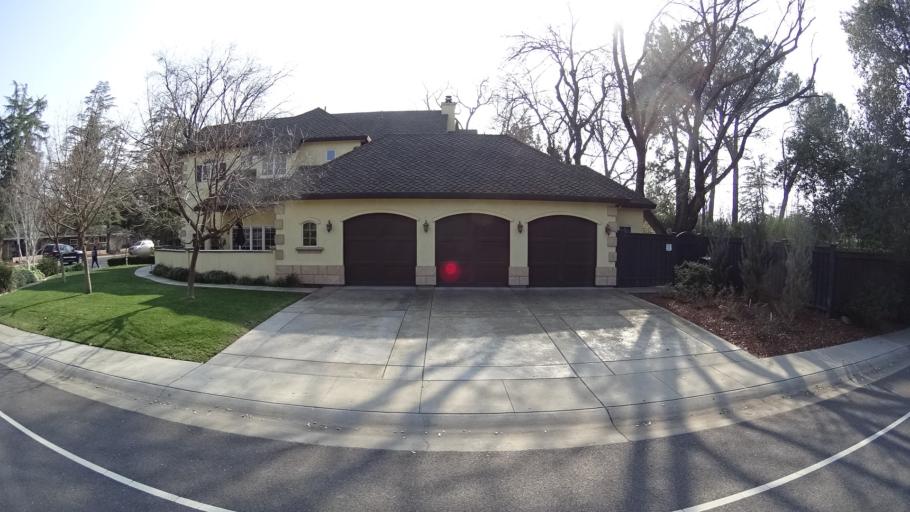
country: US
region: California
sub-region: Yolo County
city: Davis
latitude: 38.5507
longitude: -121.7532
